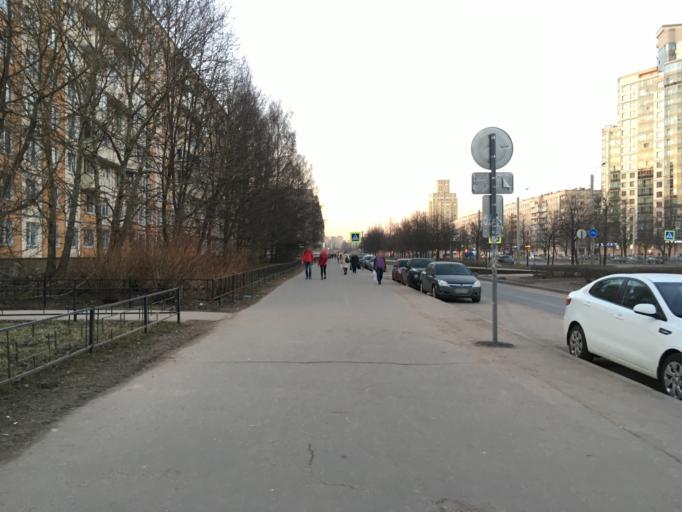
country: RU
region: St.-Petersburg
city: Grazhdanka
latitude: 60.0302
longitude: 30.4141
